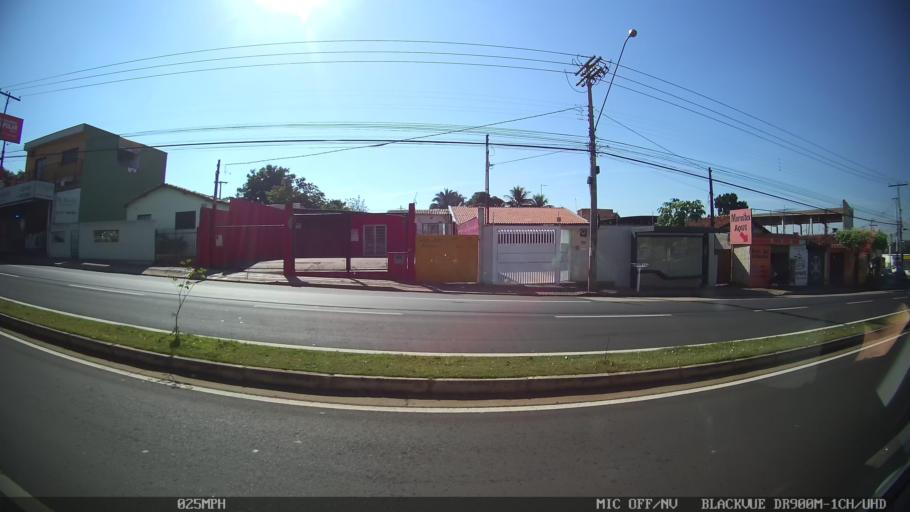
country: BR
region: Sao Paulo
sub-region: Sao Jose Do Rio Preto
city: Sao Jose do Rio Preto
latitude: -20.7868
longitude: -49.3907
